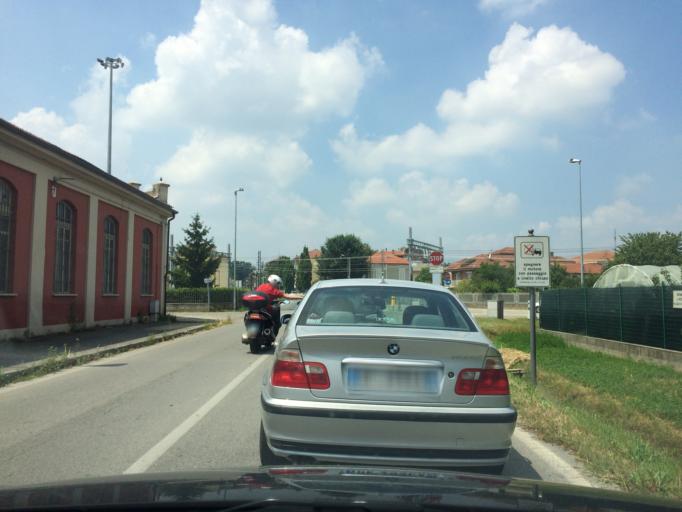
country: IT
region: Piedmont
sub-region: Provincia di Cuneo
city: Racconigi
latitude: 44.7750
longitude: 7.7010
